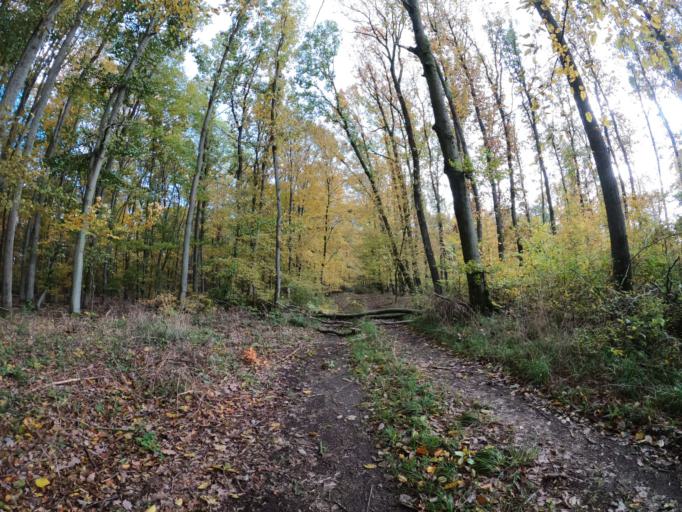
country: PL
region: West Pomeranian Voivodeship
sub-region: Powiat mysliborski
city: Barlinek
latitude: 52.9648
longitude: 15.2588
